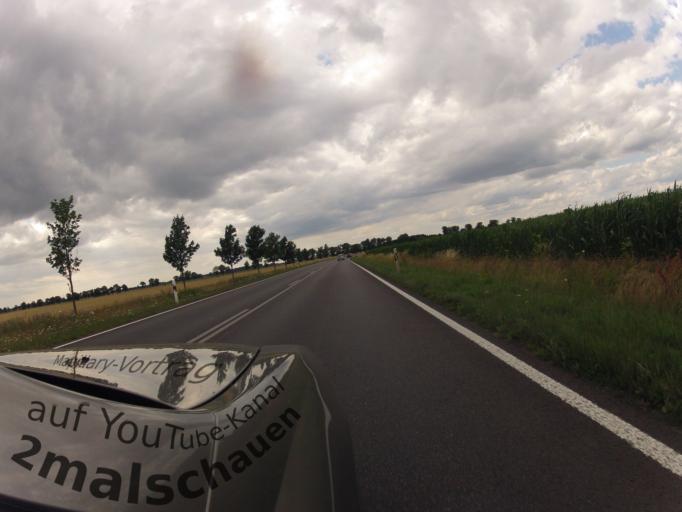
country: DE
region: Mecklenburg-Vorpommern
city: Anklam
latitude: 53.8417
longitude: 13.6683
